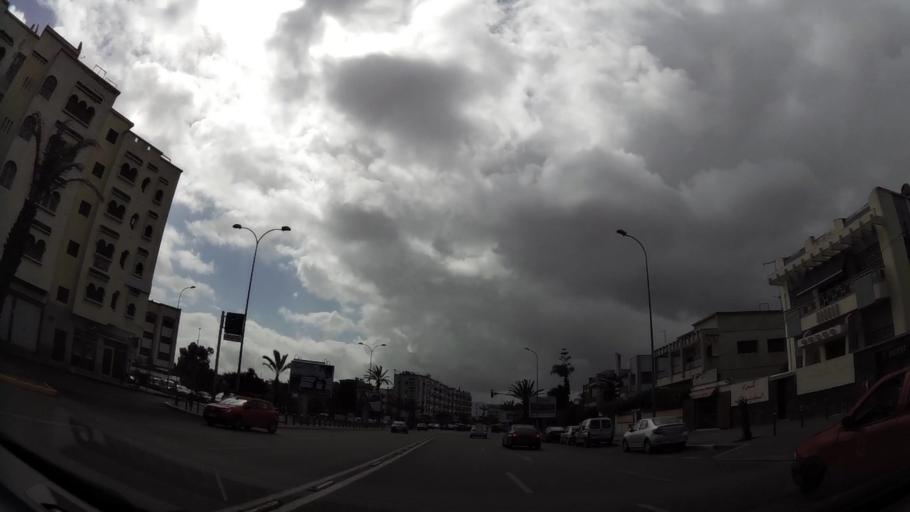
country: MA
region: Grand Casablanca
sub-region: Casablanca
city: Casablanca
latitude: 33.5518
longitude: -7.6032
